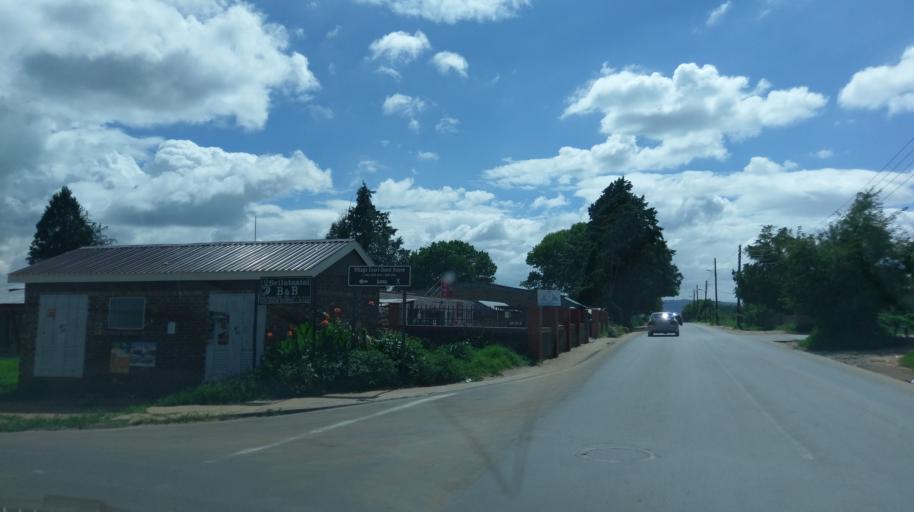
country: LS
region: Maseru
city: Maseru
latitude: -29.3101
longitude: 27.4972
